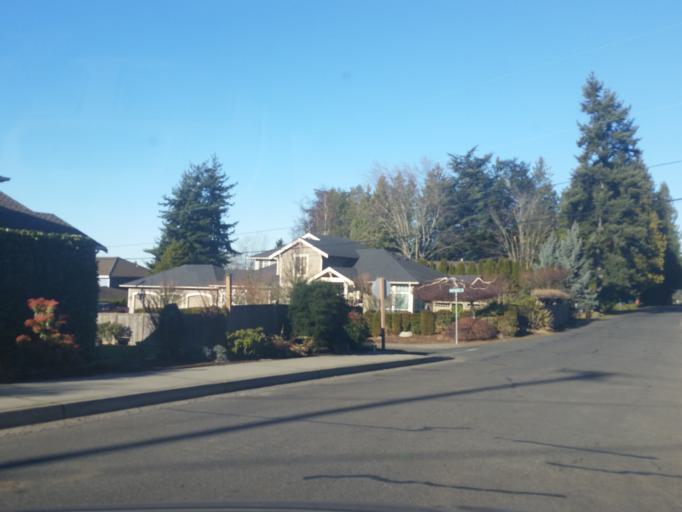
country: US
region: Washington
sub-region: Snohomish County
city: Edmonds
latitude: 47.8216
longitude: -122.3670
